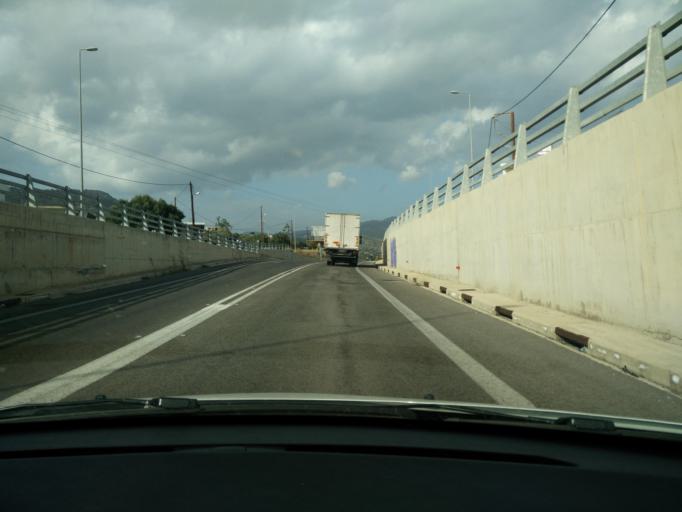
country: GR
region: Crete
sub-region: Nomos Lasithiou
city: Agios Nikolaos
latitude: 35.1860
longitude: 25.7046
